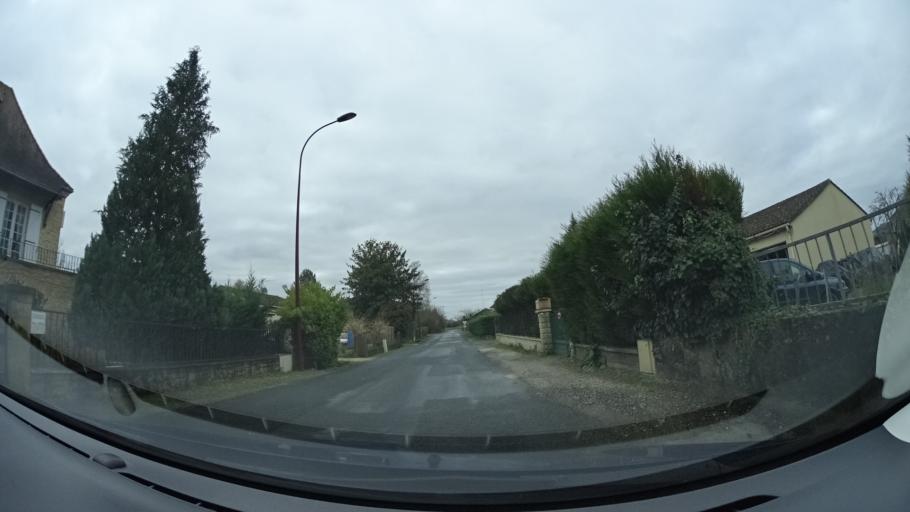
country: FR
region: Aquitaine
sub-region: Departement de la Dordogne
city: Saint-Cyprien
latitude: 44.8666
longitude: 1.0485
